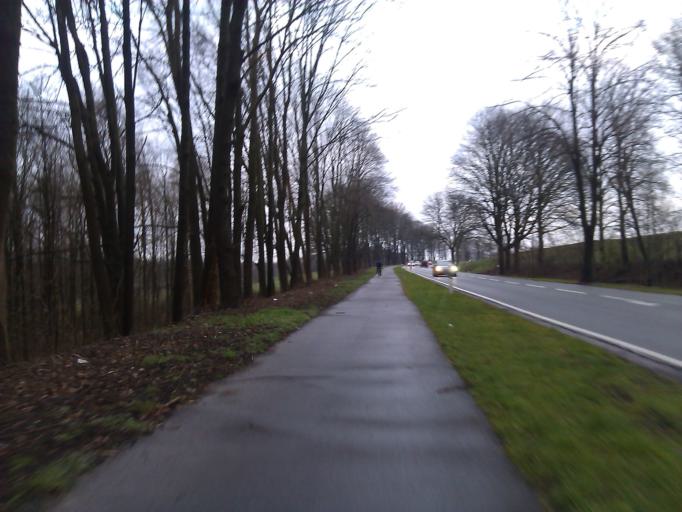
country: DE
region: North Rhine-Westphalia
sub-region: Regierungsbezirk Dusseldorf
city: Heiligenhaus
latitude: 51.3937
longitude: 6.9466
